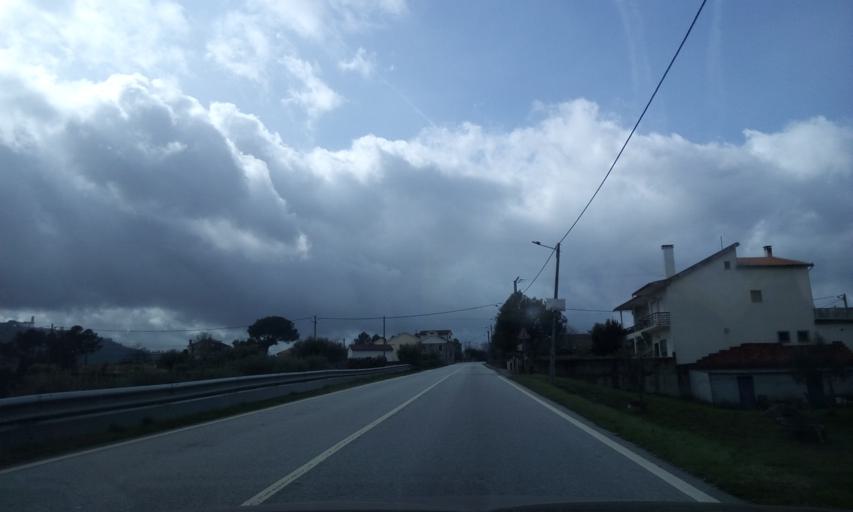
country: PT
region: Viseu
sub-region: Mangualde
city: Mangualde
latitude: 40.6307
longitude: -7.7481
